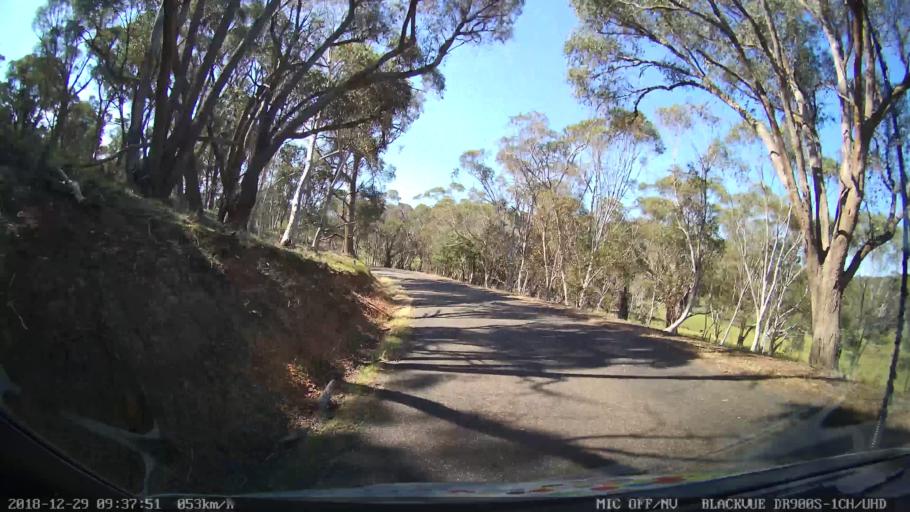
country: AU
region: New South Wales
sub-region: Upper Lachlan Shire
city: Crookwell
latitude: -34.6415
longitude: 149.3743
